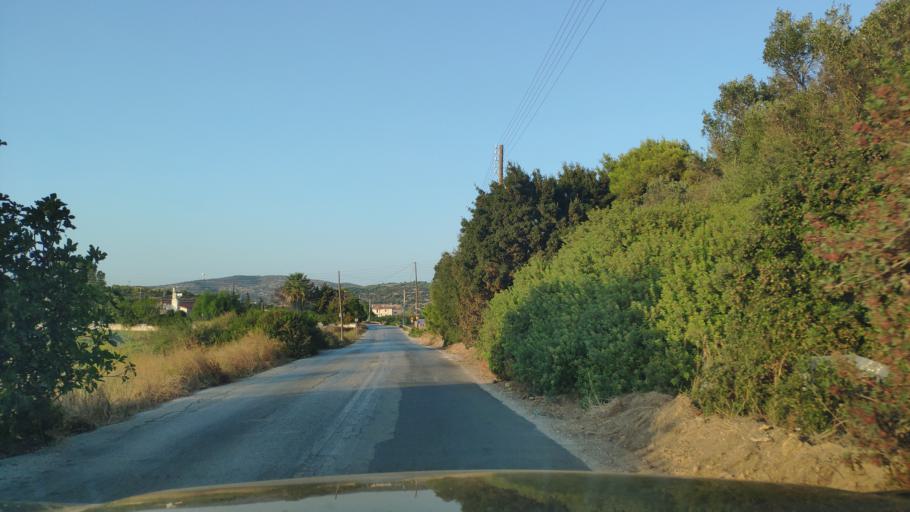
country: GR
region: Attica
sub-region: Nomarchia Anatolikis Attikis
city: Limin Mesoyaias
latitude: 37.9170
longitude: 23.9748
